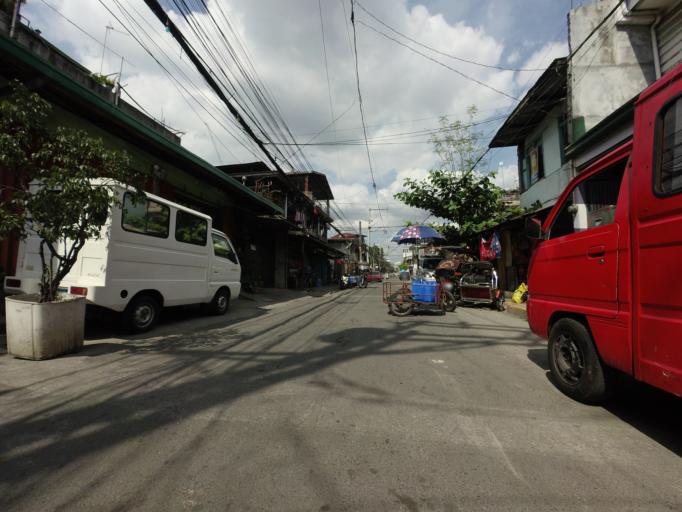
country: PH
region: Metro Manila
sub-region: City of Manila
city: Quiapo
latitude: 14.5738
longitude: 120.9958
